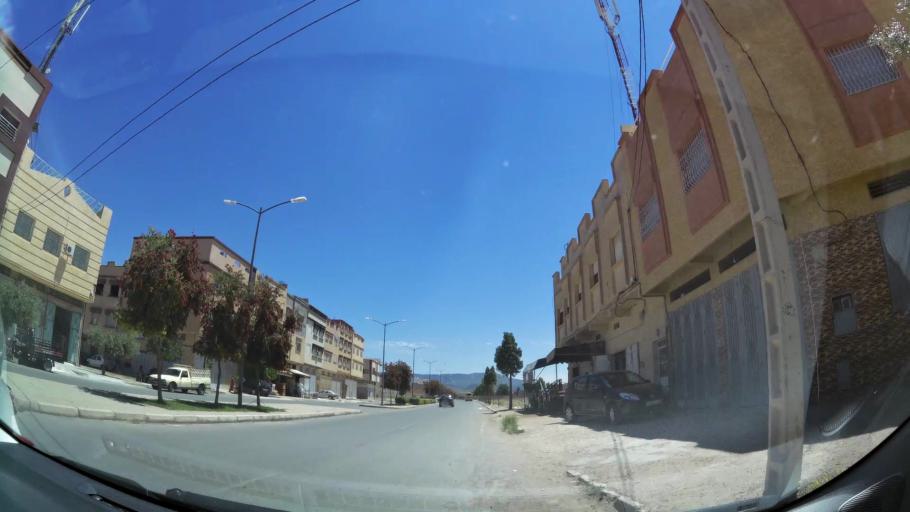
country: MA
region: Oriental
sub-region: Oujda-Angad
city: Oujda
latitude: 34.6794
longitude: -1.8700
